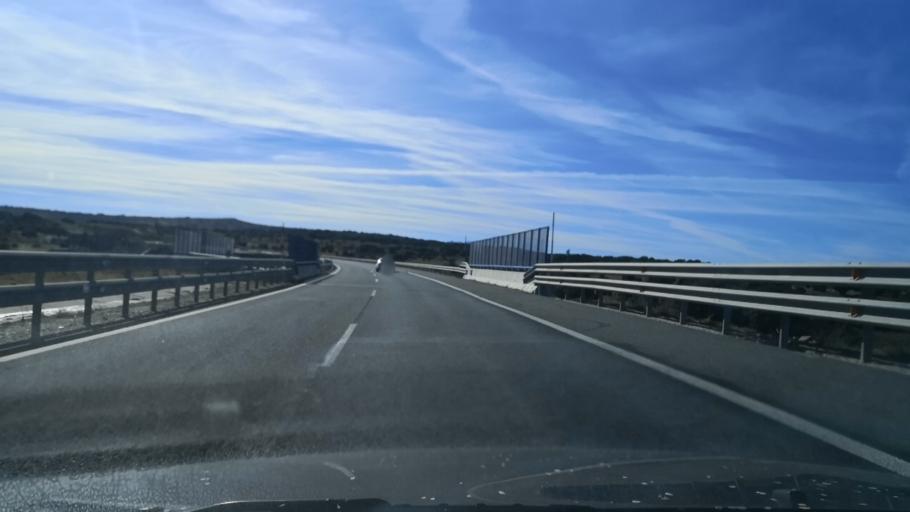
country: ES
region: Castille and Leon
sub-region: Provincia de Avila
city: Cardenosa
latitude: 40.7485
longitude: -4.7595
